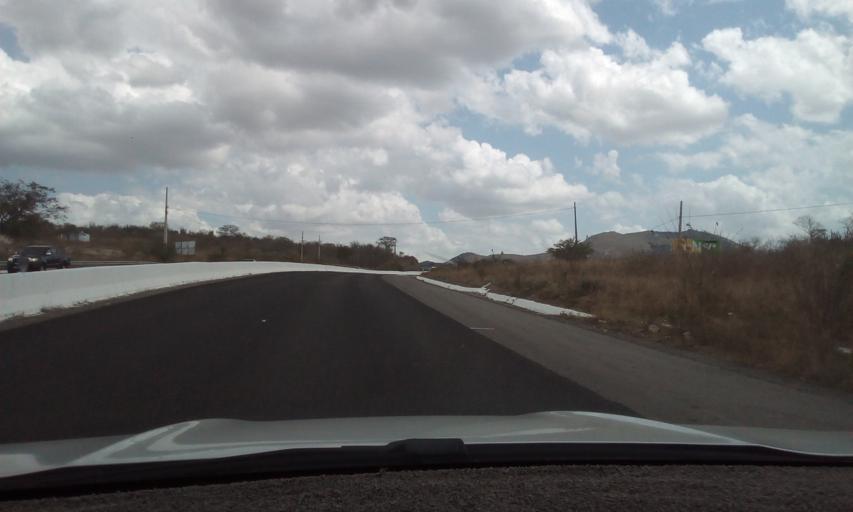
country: BR
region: Pernambuco
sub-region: Toritama
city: Toritama
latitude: -8.0667
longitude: -36.0467
